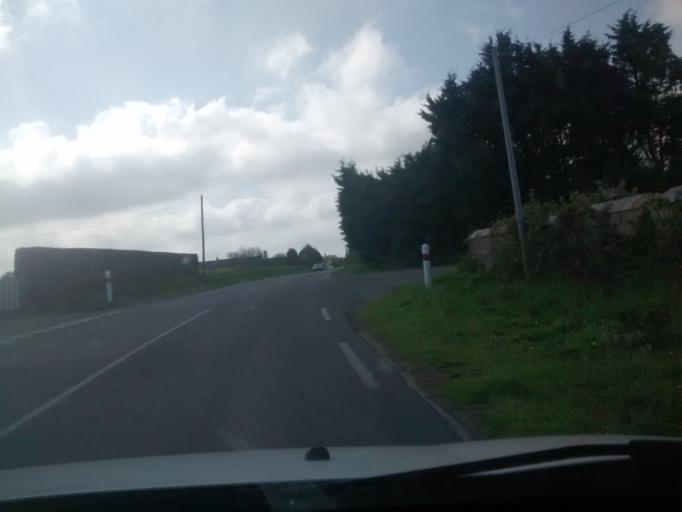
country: FR
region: Brittany
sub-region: Departement des Cotes-d'Armor
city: Louannec
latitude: 48.7899
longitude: -3.4014
